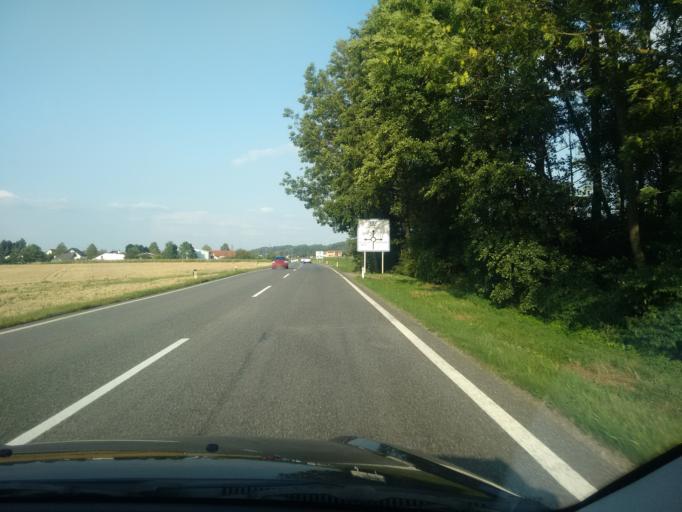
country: AT
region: Upper Austria
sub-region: Politischer Bezirk Linz-Land
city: Sankt Florian
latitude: 48.1994
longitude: 14.3752
